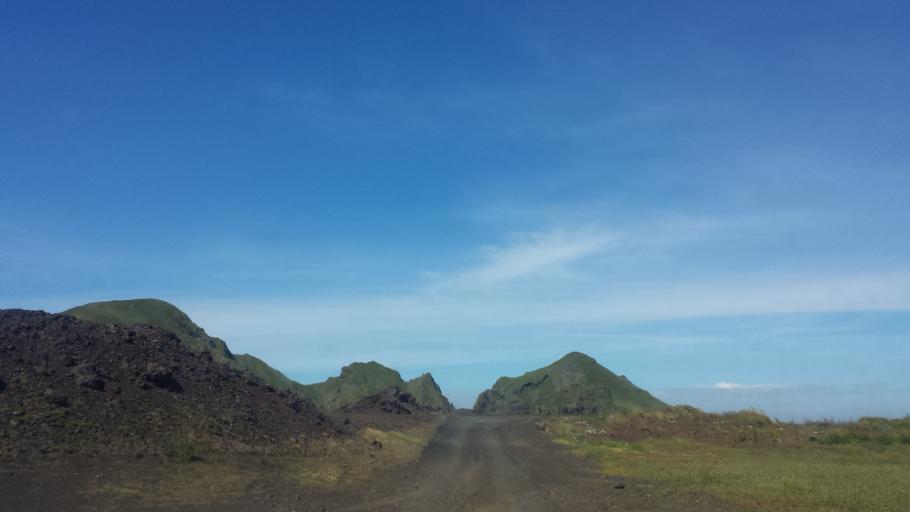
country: IS
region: South
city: Vestmannaeyjar
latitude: 63.4384
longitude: -20.2454
